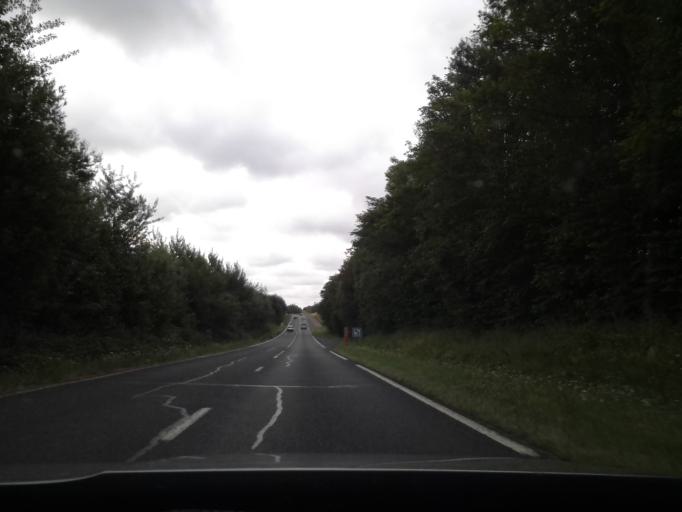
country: FR
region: Lower Normandy
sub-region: Departement du Calvados
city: Le Molay-Littry
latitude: 49.3159
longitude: -0.8450
